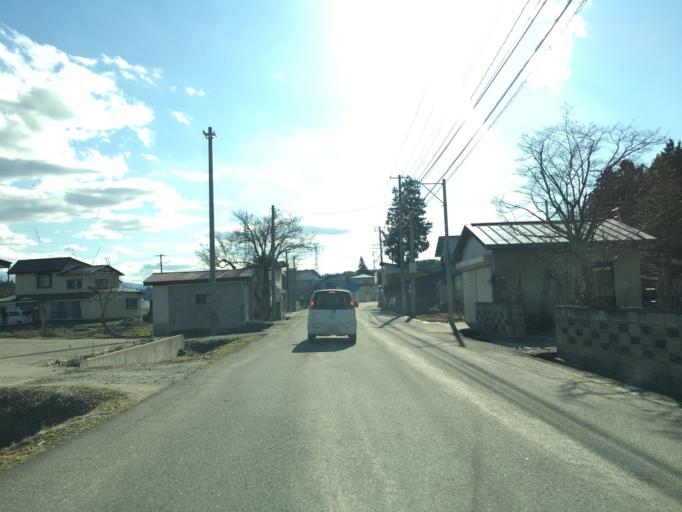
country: JP
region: Yamagata
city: Nagai
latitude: 37.9992
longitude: 140.0157
